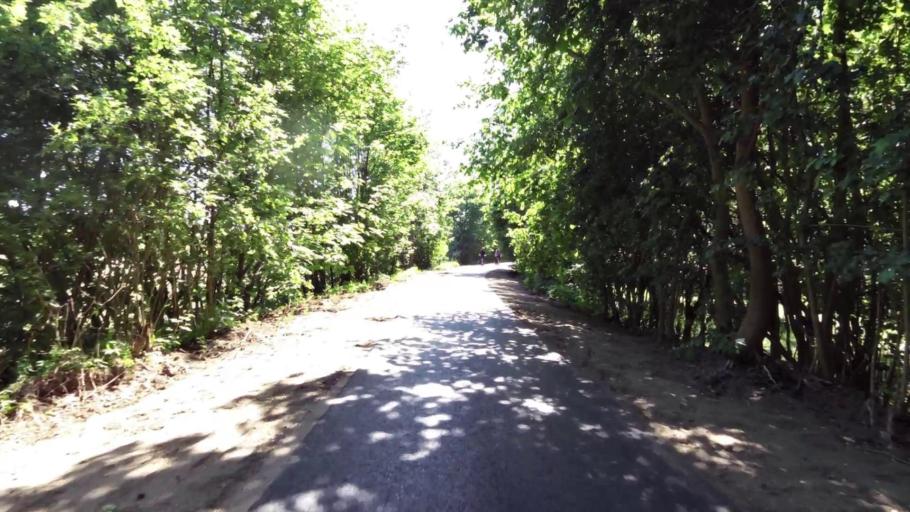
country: PL
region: West Pomeranian Voivodeship
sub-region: Powiat gryfinski
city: Gryfino
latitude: 53.2237
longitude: 14.5532
